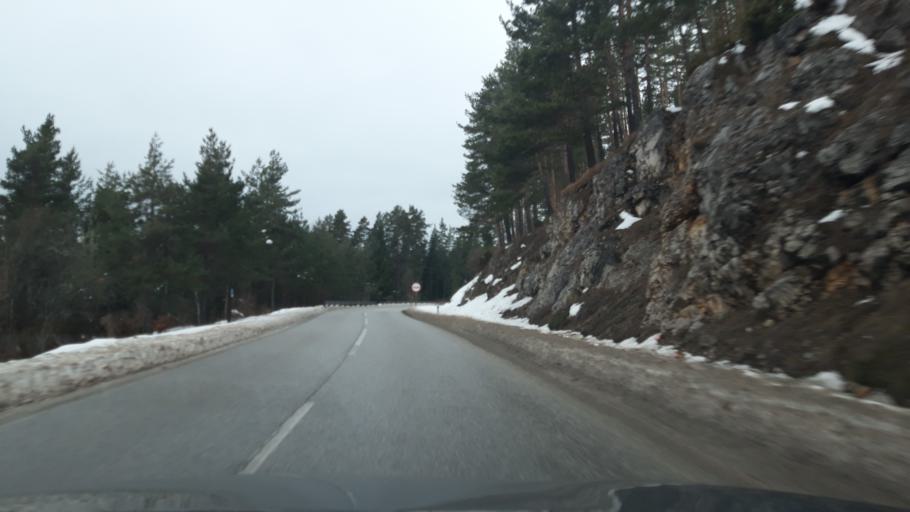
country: BA
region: Republika Srpska
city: Sokolac
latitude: 43.9097
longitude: 18.7157
